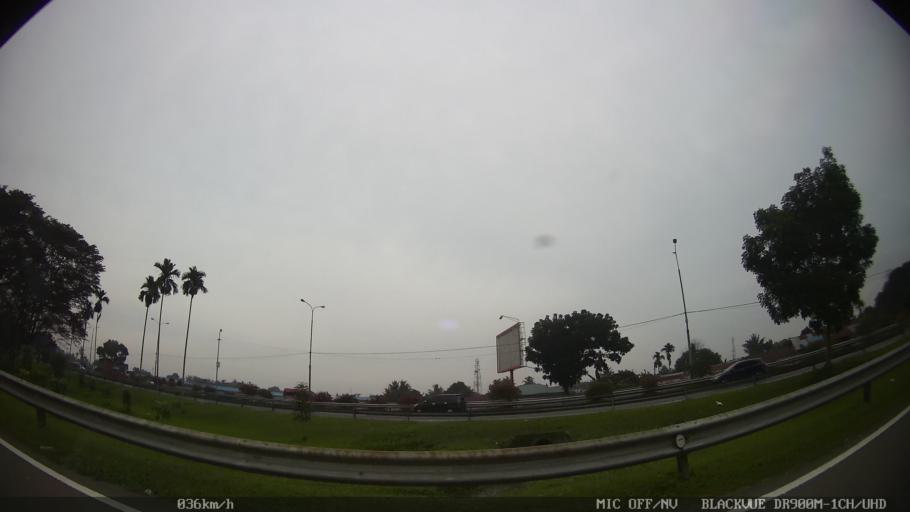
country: ID
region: North Sumatra
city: Deli Tua
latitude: 3.5477
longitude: 98.7250
